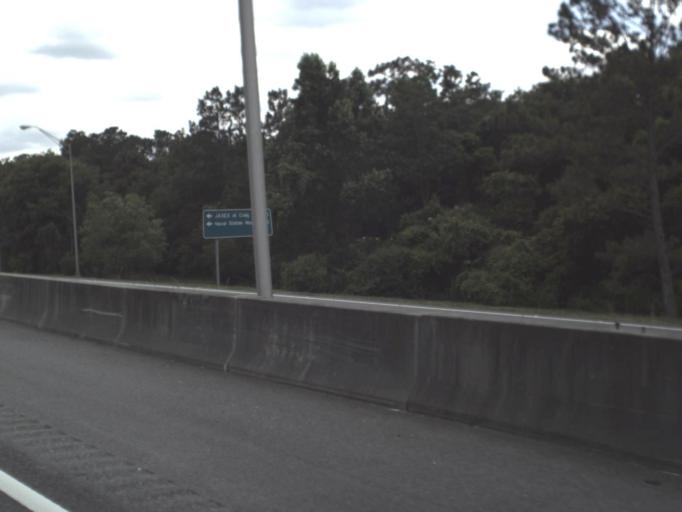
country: US
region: Florida
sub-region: Duval County
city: Jacksonville
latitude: 30.3268
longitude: -81.5287
